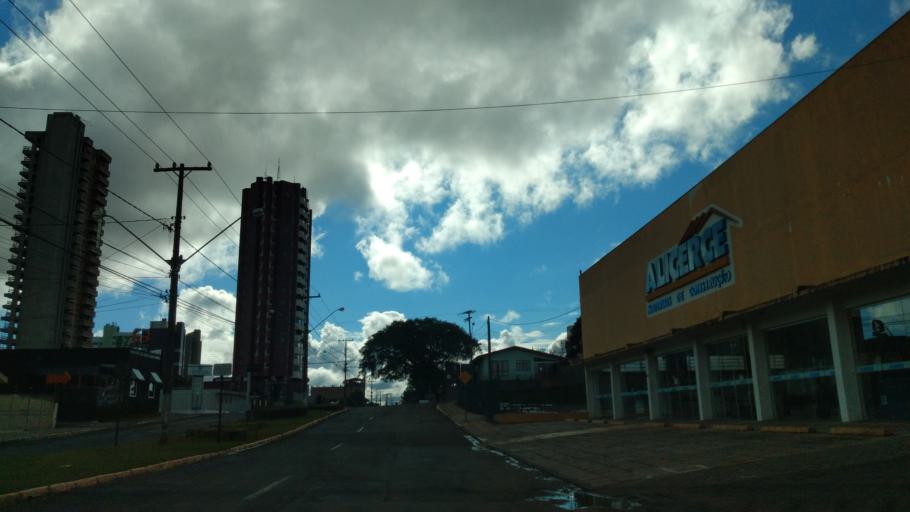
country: BR
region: Parana
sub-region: Guarapuava
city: Guarapuava
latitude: -25.3899
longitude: -51.4600
